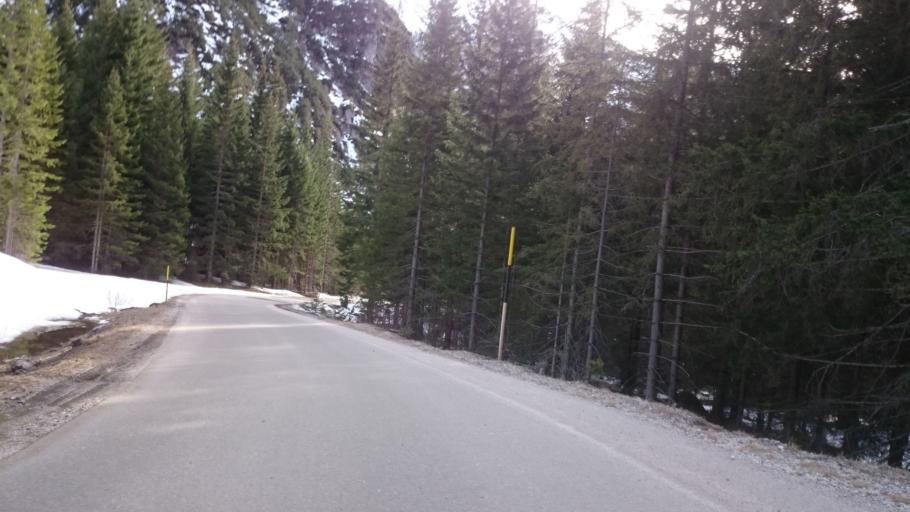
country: IT
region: Trentino-Alto Adige
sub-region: Bolzano
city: Braies
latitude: 46.6722
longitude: 12.1516
